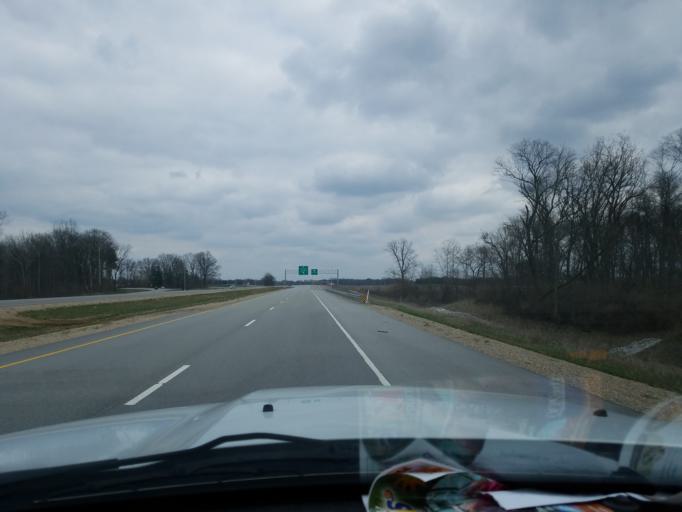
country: US
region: Indiana
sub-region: Vigo County
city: Terre Haute
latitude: 39.4122
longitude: -87.3431
